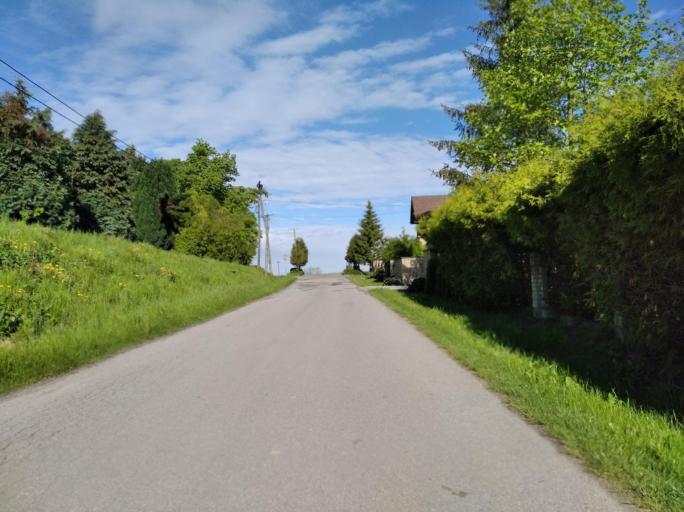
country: PL
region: Subcarpathian Voivodeship
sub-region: Powiat strzyzowski
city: Frysztak
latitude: 49.8479
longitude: 21.5286
